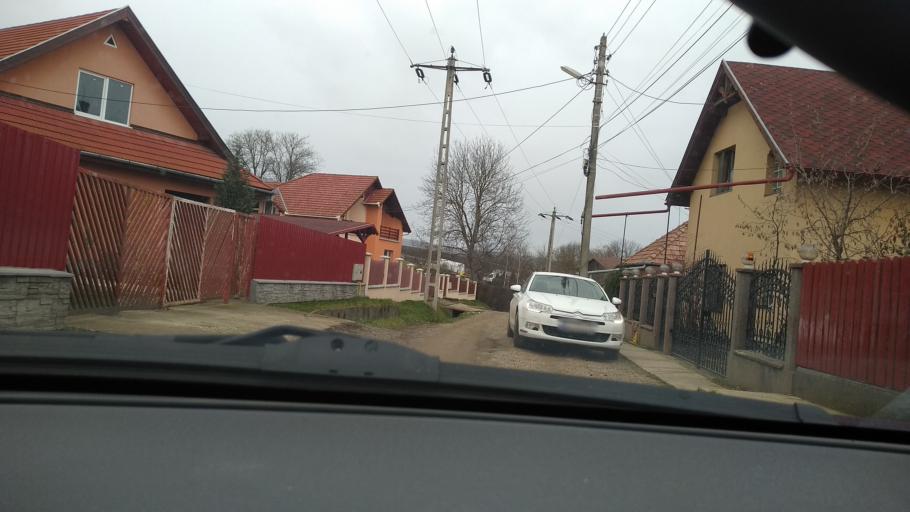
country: RO
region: Mures
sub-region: Comuna Panet
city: Panet
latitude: 46.5492
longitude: 24.4671
